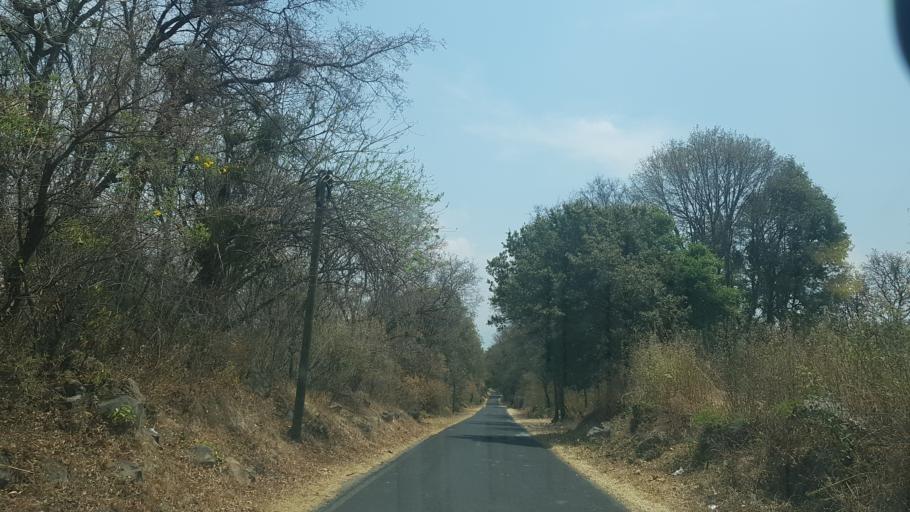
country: MX
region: Puebla
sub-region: Tochimilco
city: La Magdalena Yancuitlalpan
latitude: 18.8865
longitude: -98.5970
